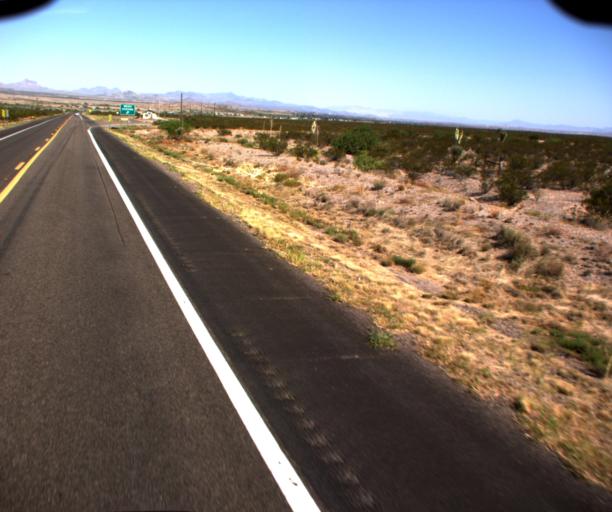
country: US
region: Arizona
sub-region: Greenlee County
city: Clifton
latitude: 32.6545
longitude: -109.0607
